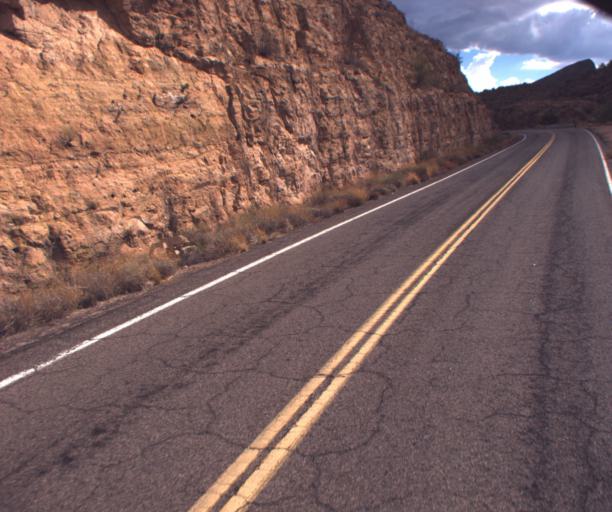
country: US
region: Arizona
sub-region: Pinal County
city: Apache Junction
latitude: 33.5333
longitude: -111.3696
